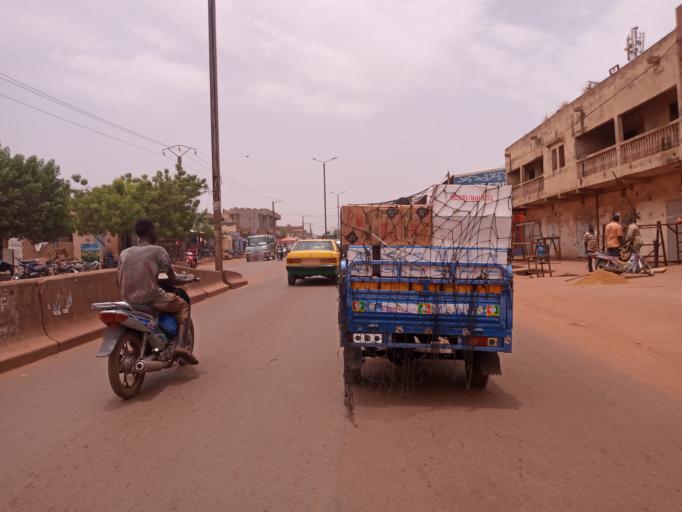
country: ML
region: Bamako
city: Bamako
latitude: 12.5941
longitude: -8.0178
